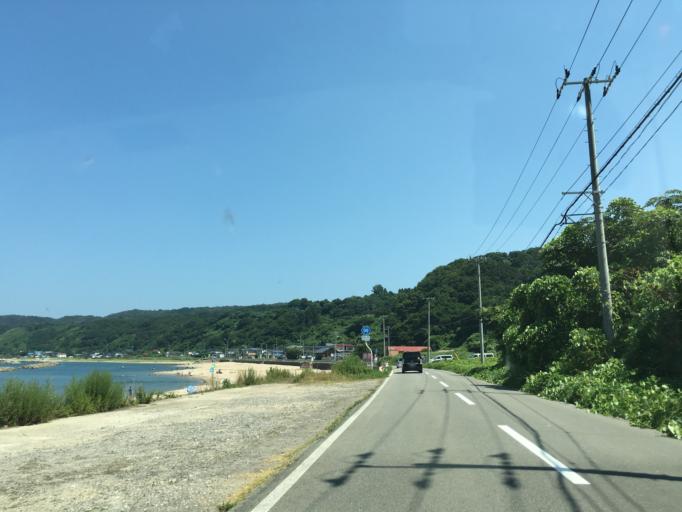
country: JP
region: Akita
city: Tenno
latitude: 39.9454
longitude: 139.7182
